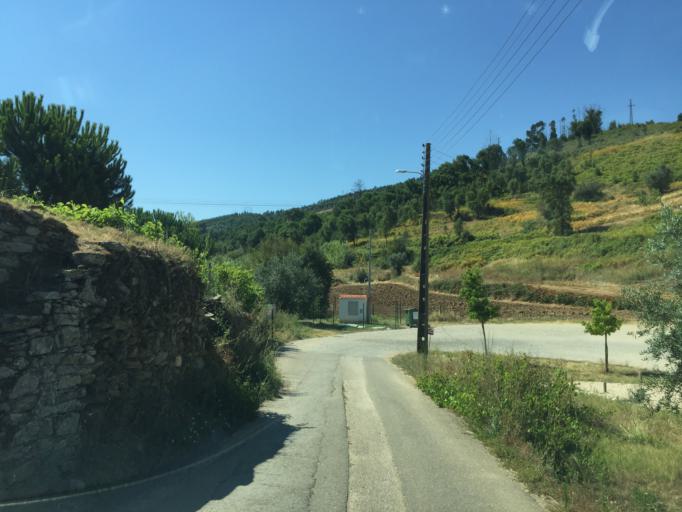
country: PT
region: Santarem
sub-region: Constancia
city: Constancia
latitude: 39.5435
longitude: -8.2747
